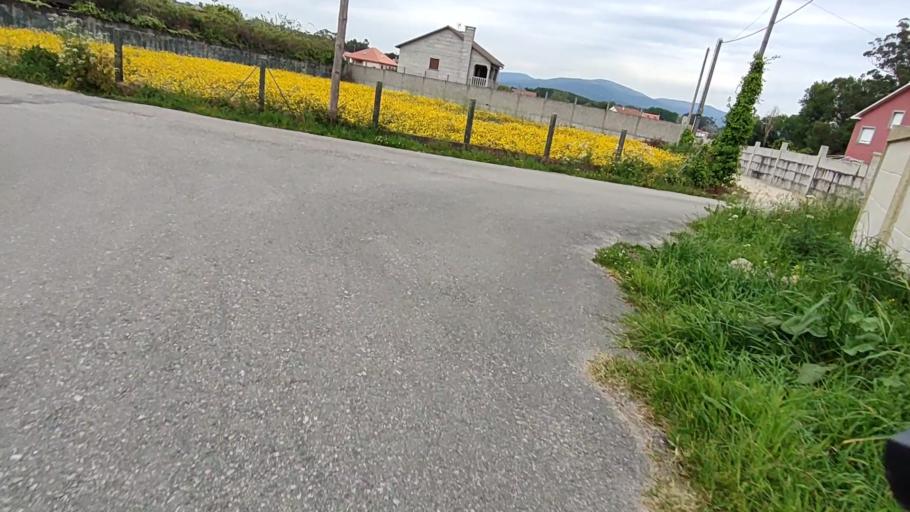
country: ES
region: Galicia
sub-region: Provincia da Coruna
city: Boiro
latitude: 42.6322
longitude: -8.8630
